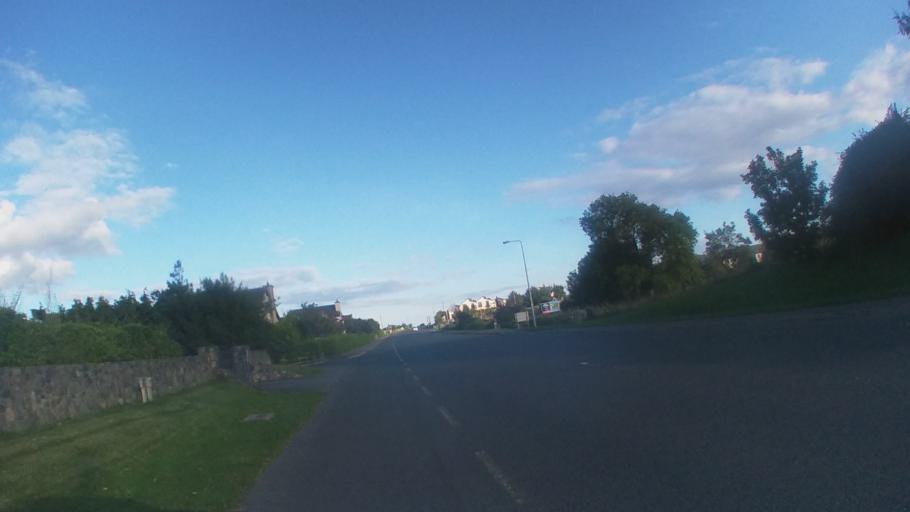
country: IE
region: Leinster
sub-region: Lu
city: Carlingford
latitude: 54.0391
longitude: -6.1783
